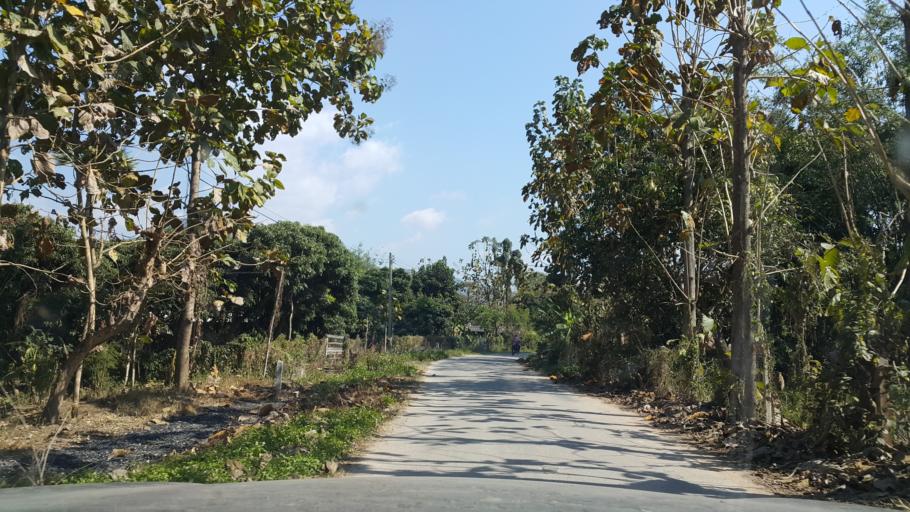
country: TH
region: Chiang Mai
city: Mae On
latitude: 18.7270
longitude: 99.2148
